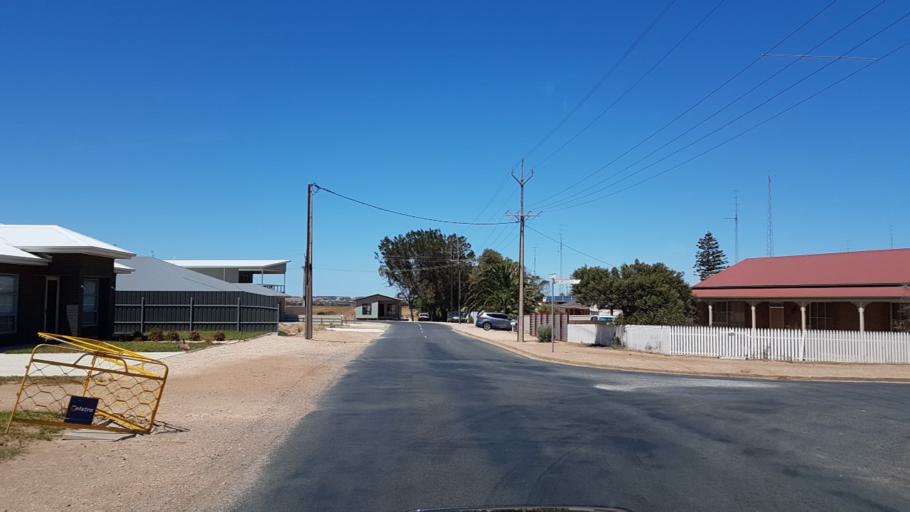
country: AU
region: South Australia
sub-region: Copper Coast
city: Wallaroo
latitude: -33.8958
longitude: 137.6297
